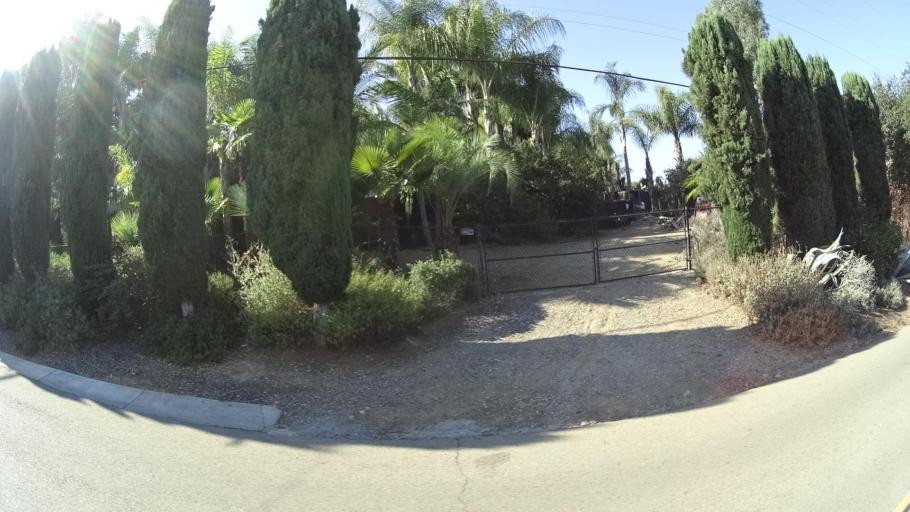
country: US
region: California
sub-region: San Diego County
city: Fallbrook
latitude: 33.3912
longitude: -117.2356
